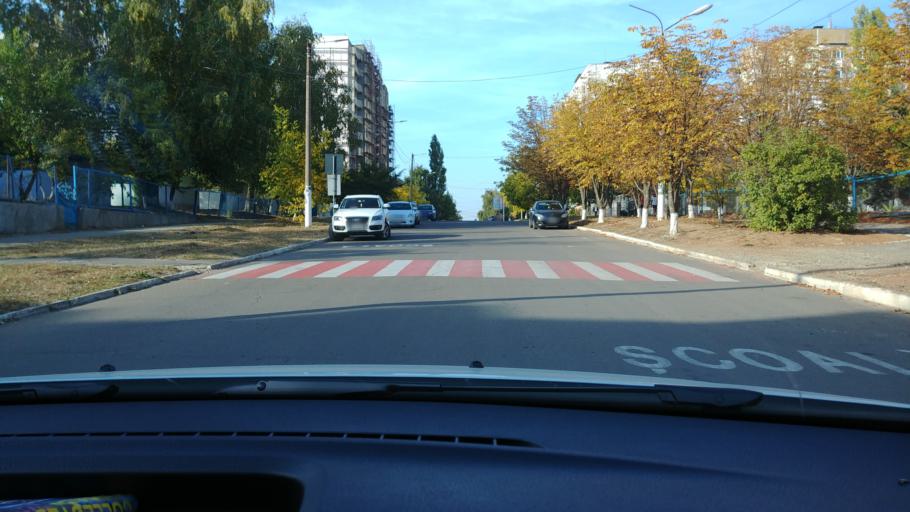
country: MD
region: Rezina
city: Rezina
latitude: 47.7468
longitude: 28.9561
